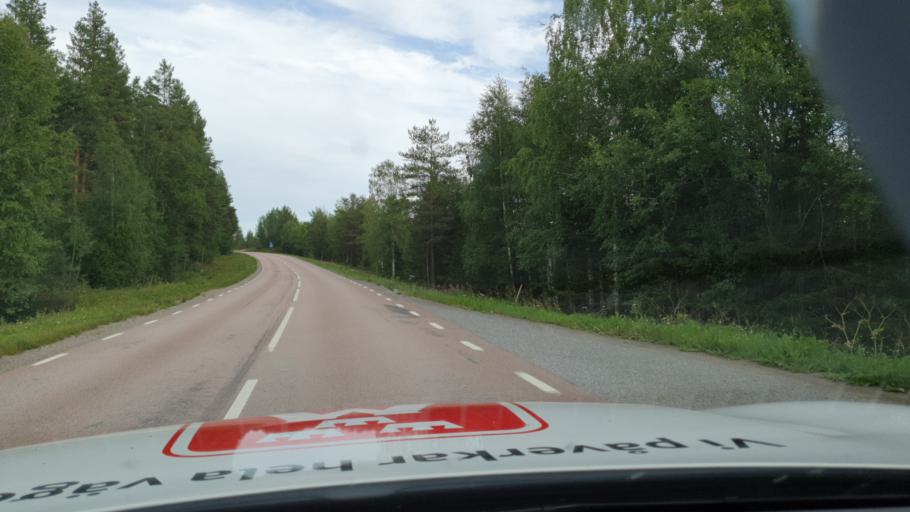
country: SE
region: Vaesternorrland
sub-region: Solleftea Kommun
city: As
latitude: 63.5781
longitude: 16.3658
